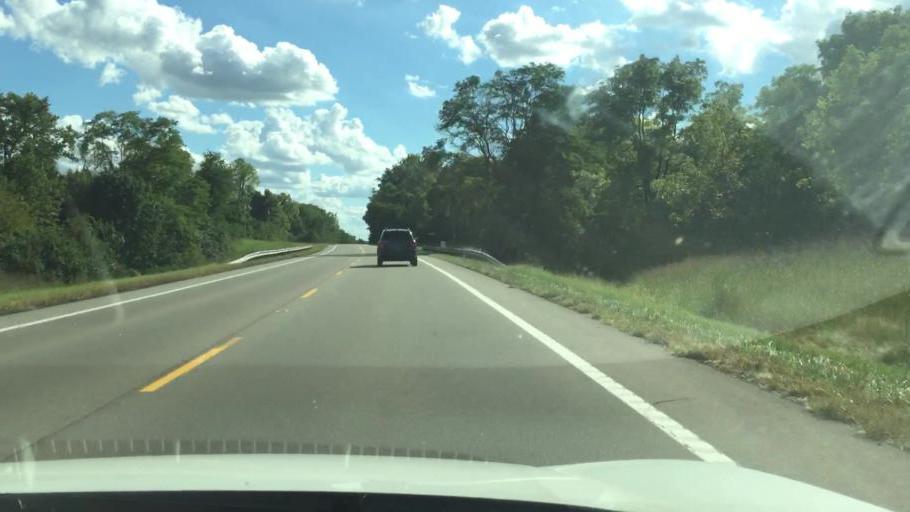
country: US
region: Ohio
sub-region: Clark County
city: Northridge
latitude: 39.9941
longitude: -83.7295
